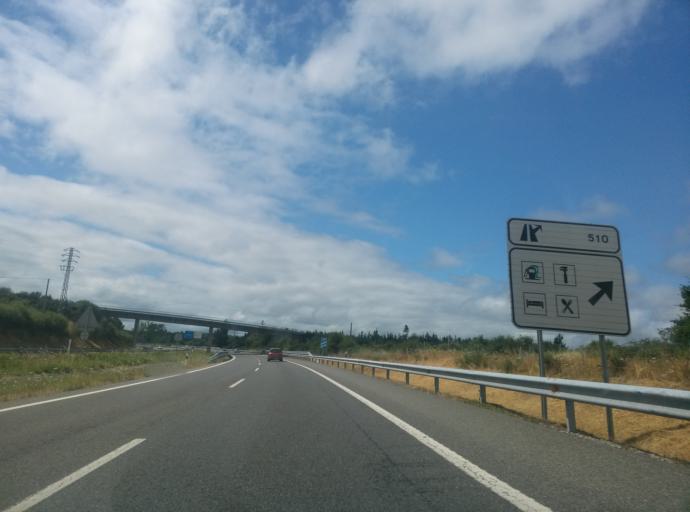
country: ES
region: Galicia
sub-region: Provincia de Lugo
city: Rabade
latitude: 43.1258
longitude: -7.6150
